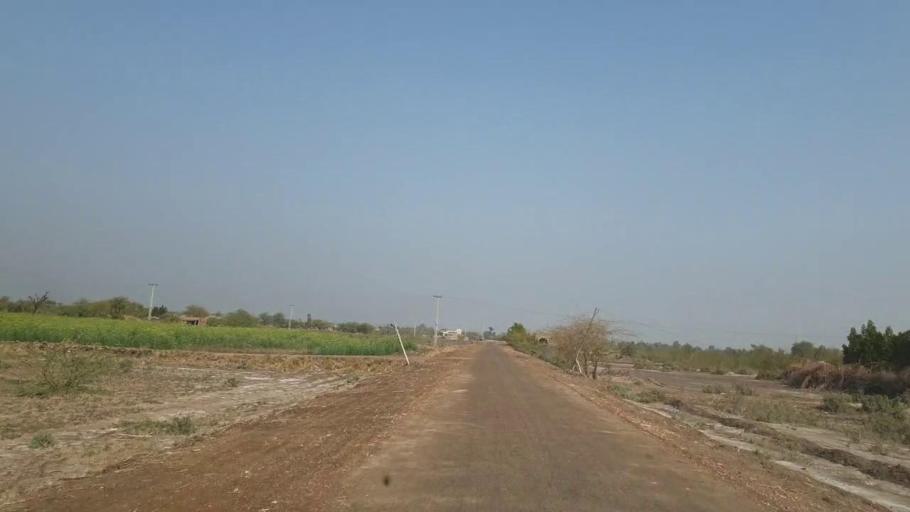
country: PK
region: Sindh
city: Mirpur Khas
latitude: 25.5932
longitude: 69.0148
